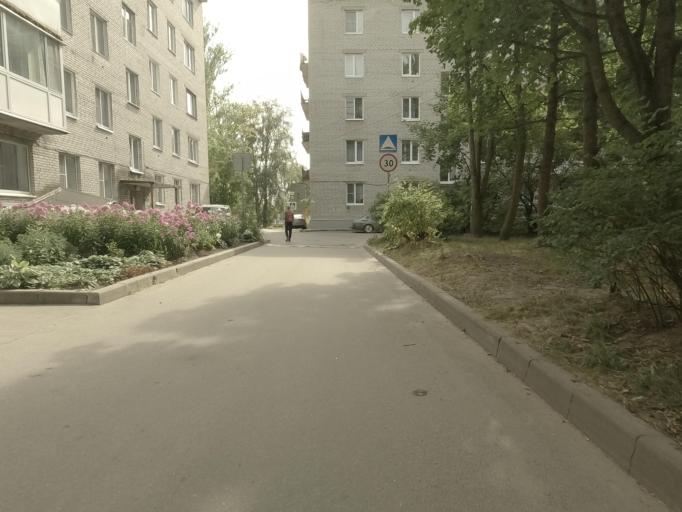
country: RU
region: Leningrad
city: Kamennogorsk
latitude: 60.9544
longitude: 29.1315
